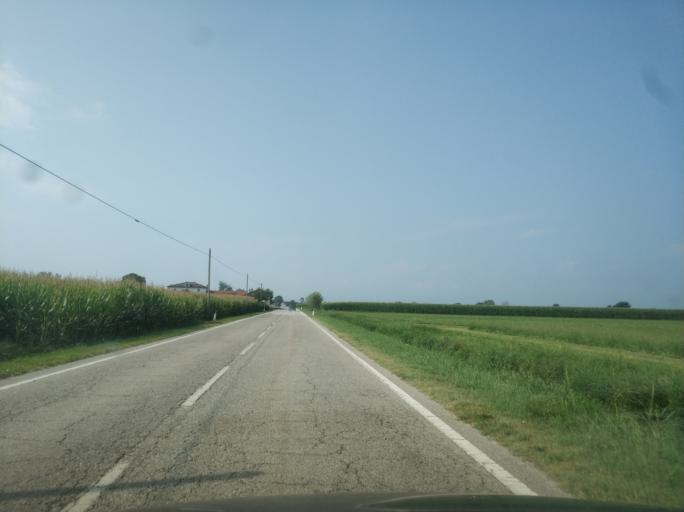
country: IT
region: Piedmont
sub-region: Provincia di Cuneo
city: Sant'Albano Stura
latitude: 44.5213
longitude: 7.6760
